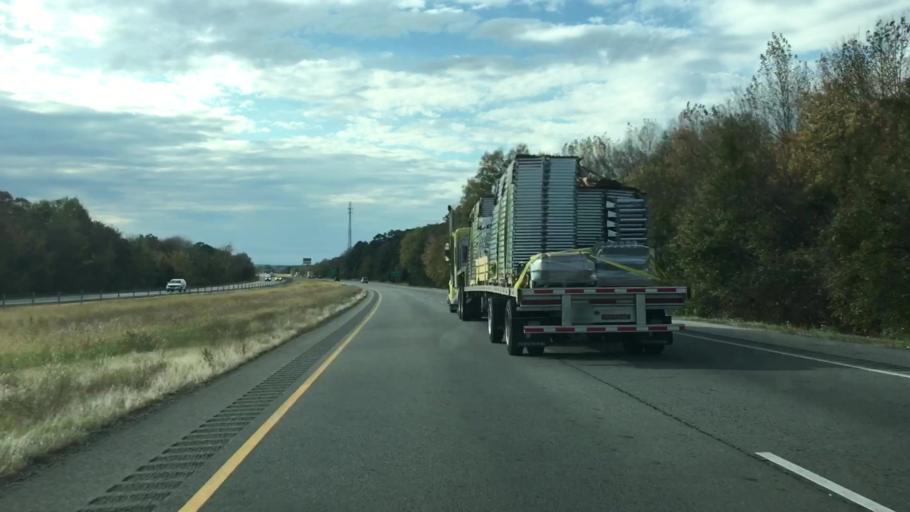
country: US
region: Arkansas
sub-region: Pope County
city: Pottsville
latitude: 35.2476
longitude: -93.0077
